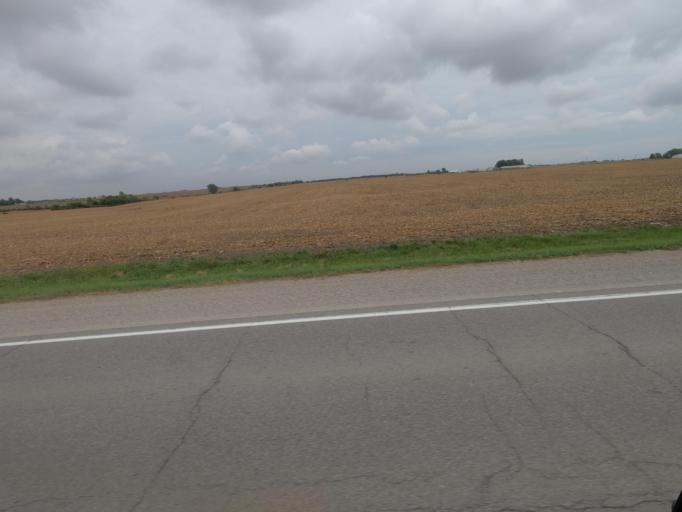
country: US
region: Iowa
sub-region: Wapello County
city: Ottumwa
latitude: 40.9540
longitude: -92.2365
